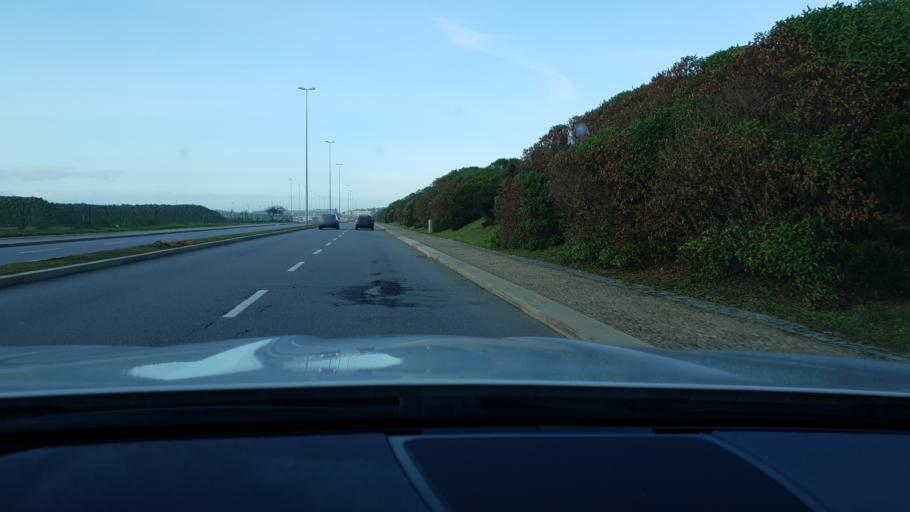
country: PT
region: Porto
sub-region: Matosinhos
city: Leca da Palmeira
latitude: 41.2128
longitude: -8.7132
